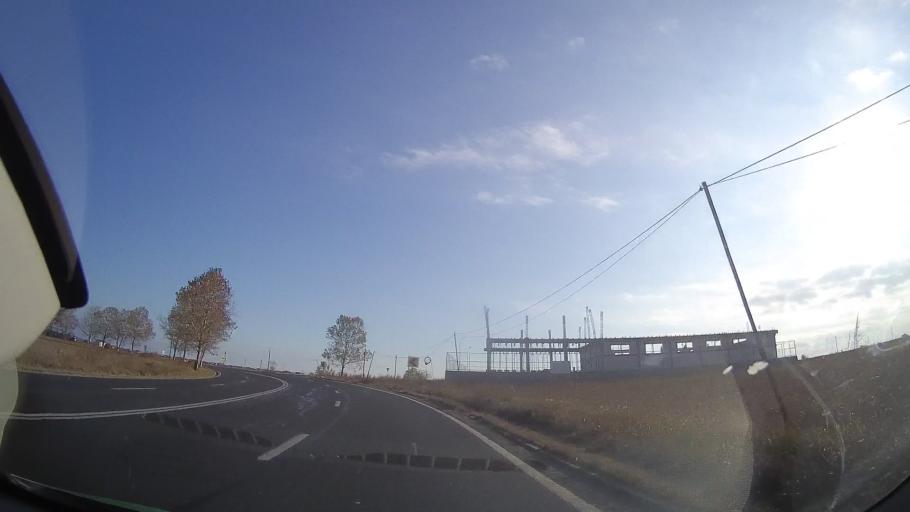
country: RO
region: Constanta
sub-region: Municipiul Mangalia
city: Mangalia
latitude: 43.7939
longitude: 28.5607
